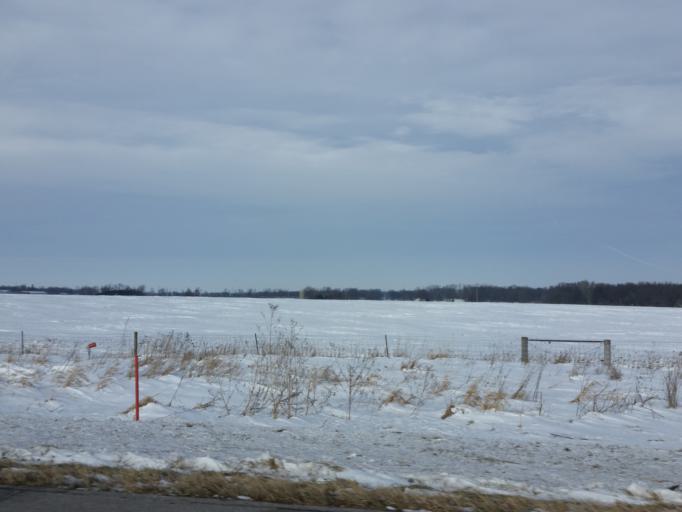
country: US
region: Iowa
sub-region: Buchanan County
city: Independence
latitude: 42.4612
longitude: -91.7196
